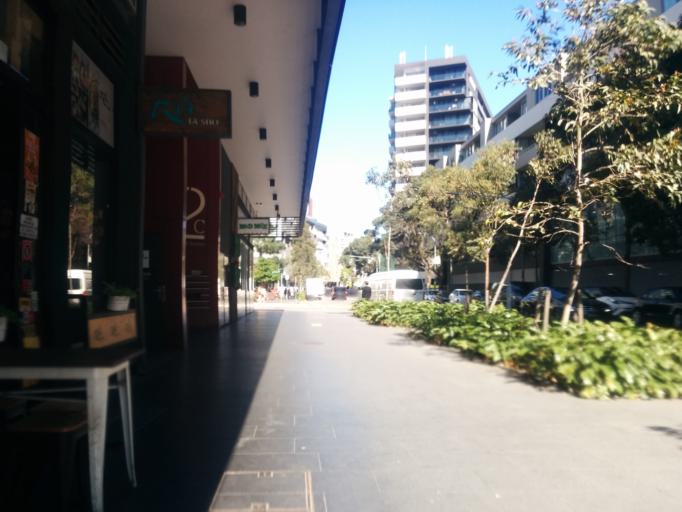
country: AU
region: New South Wales
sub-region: City of Sydney
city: Alexandria
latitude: -33.9056
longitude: 151.2125
